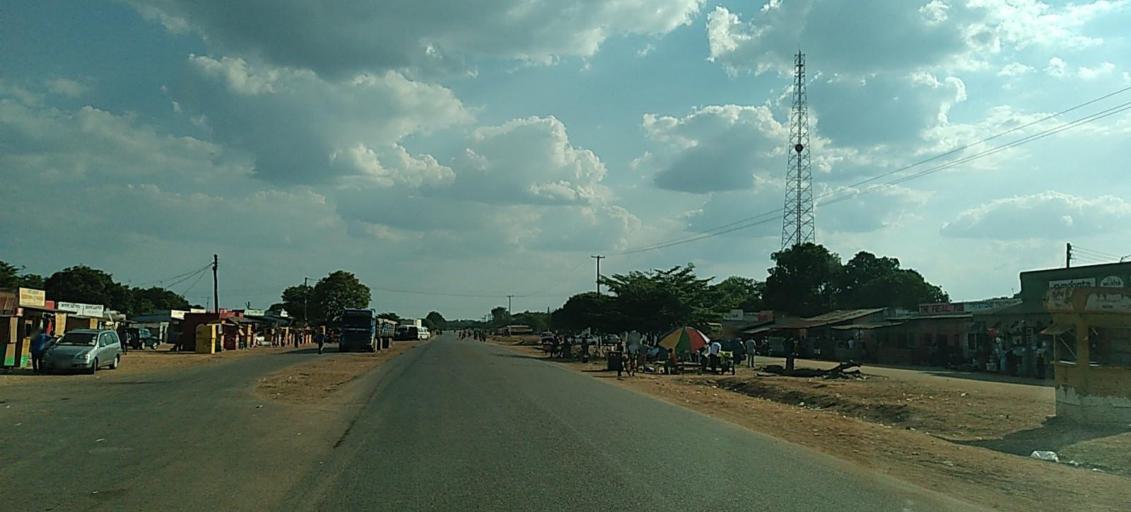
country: ZM
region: Copperbelt
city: Luanshya
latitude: -13.3561
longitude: 28.4157
